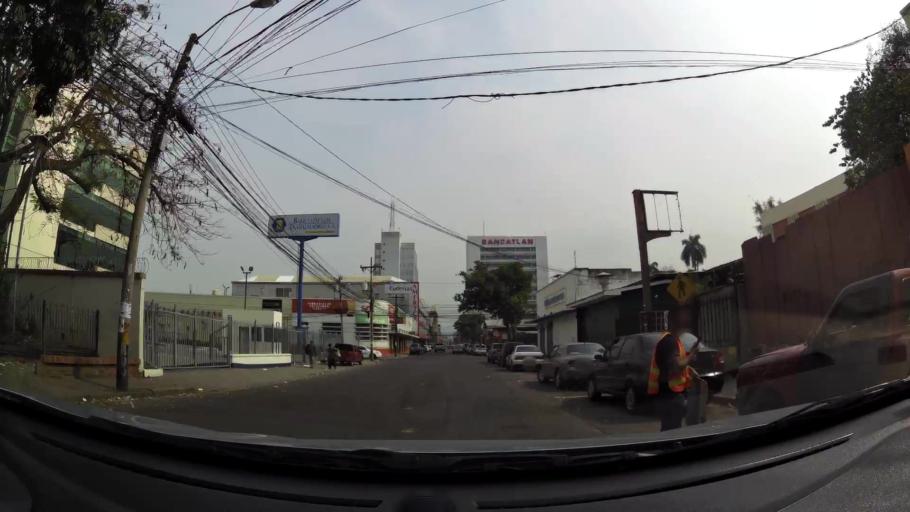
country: HN
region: Cortes
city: San Pedro Sula
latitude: 15.5080
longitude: -88.0243
